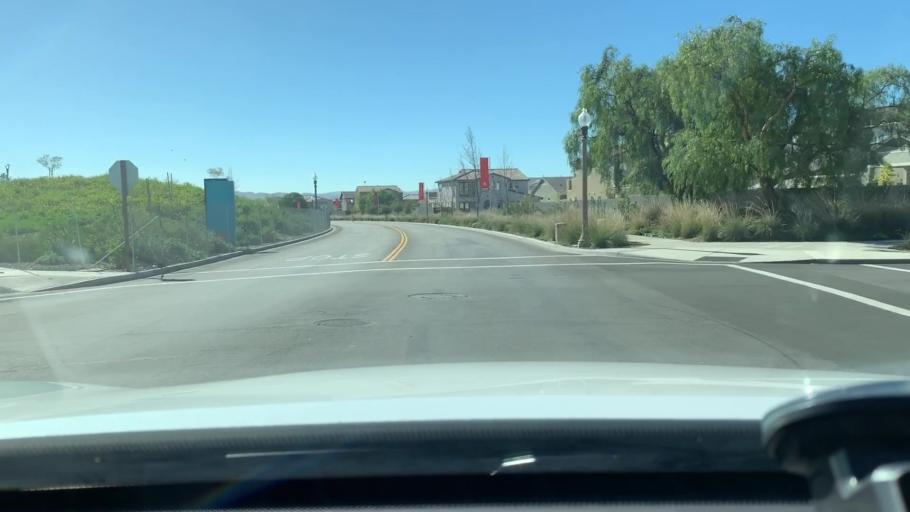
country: US
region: California
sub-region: Orange County
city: Lake Forest
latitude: 33.6869
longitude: -117.7298
